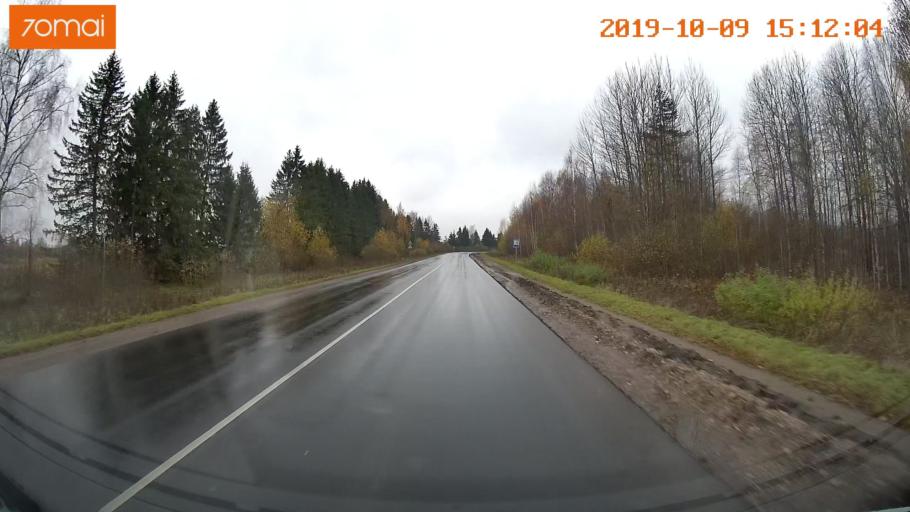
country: RU
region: Kostroma
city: Susanino
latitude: 58.1578
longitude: 41.6242
